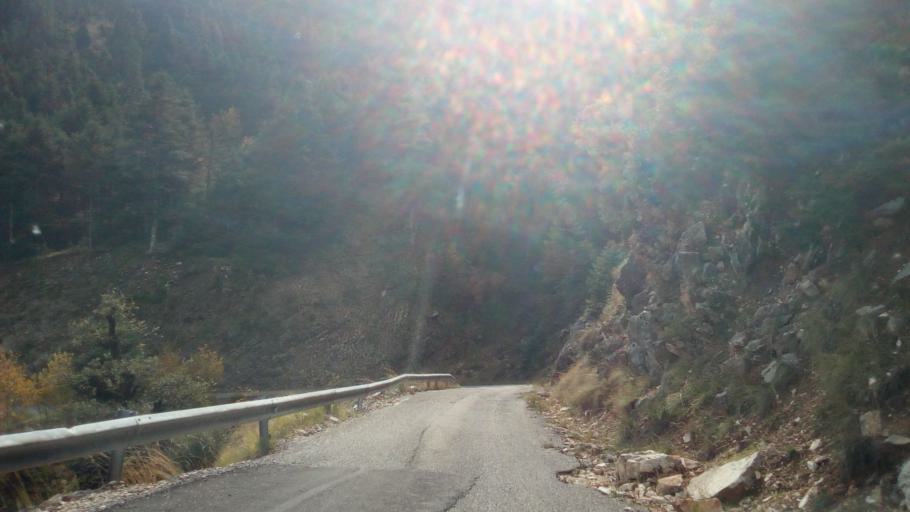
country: GR
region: West Greece
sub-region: Nomos Aitolias kai Akarnanias
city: Thermo
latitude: 38.5691
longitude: 21.8241
